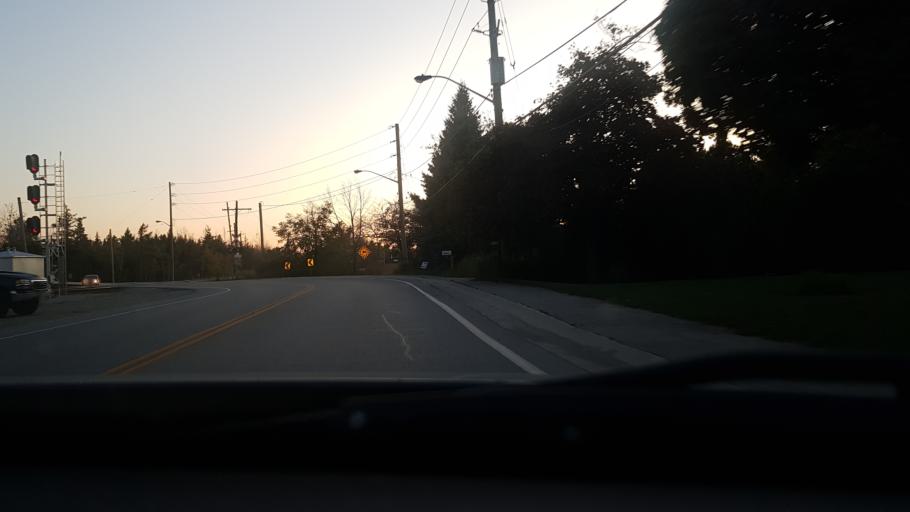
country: CA
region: Ontario
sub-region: Halton
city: Milton
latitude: 43.4799
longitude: -79.9884
